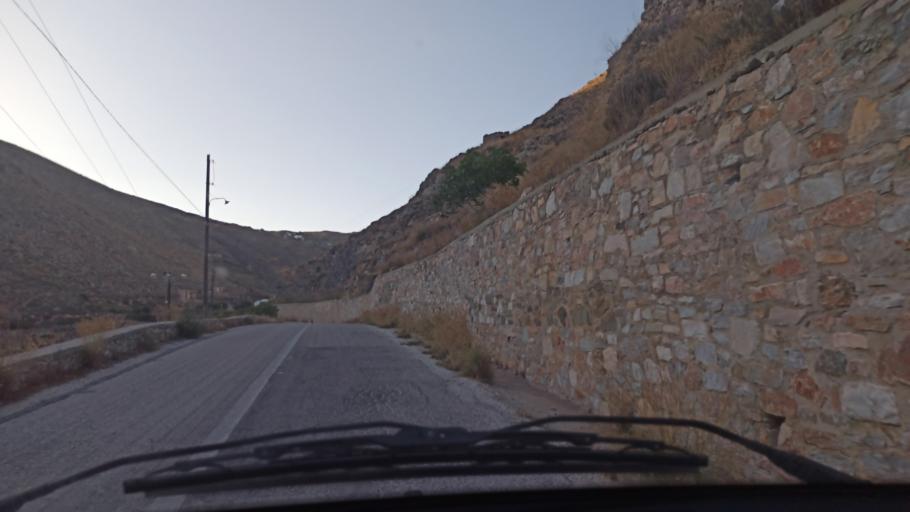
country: GR
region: South Aegean
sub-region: Nomos Kykladon
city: Ano Syros
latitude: 37.4556
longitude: 24.9331
